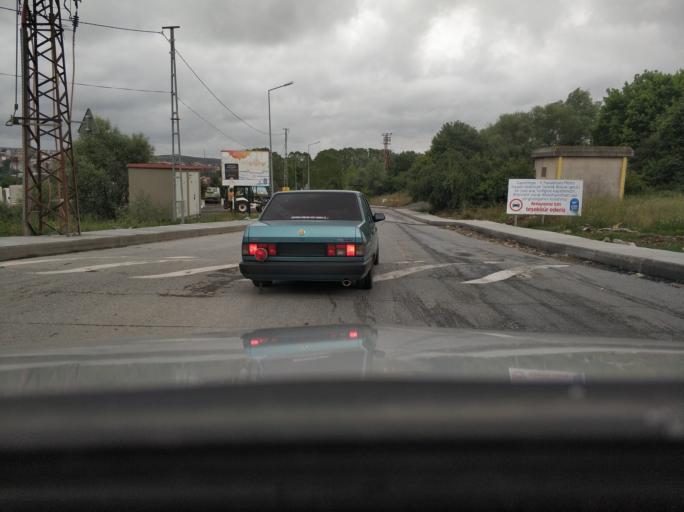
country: TR
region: Istanbul
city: Kemerburgaz
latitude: 41.1619
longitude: 28.8974
